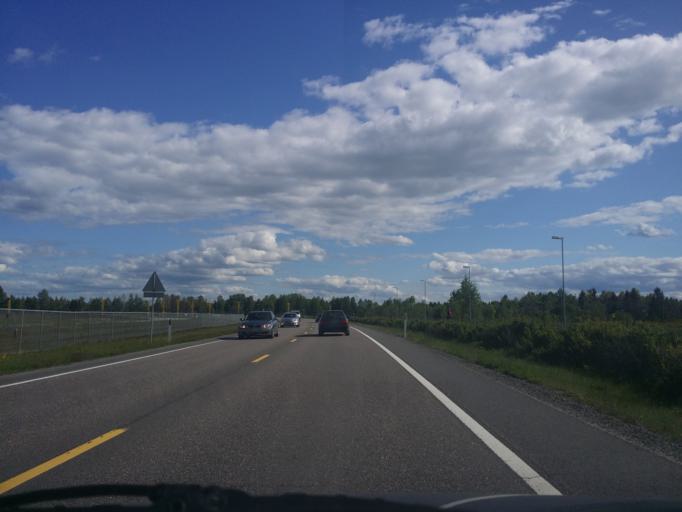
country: NO
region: Akershus
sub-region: Nannestad
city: Teigebyen
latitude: 60.1829
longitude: 11.0693
